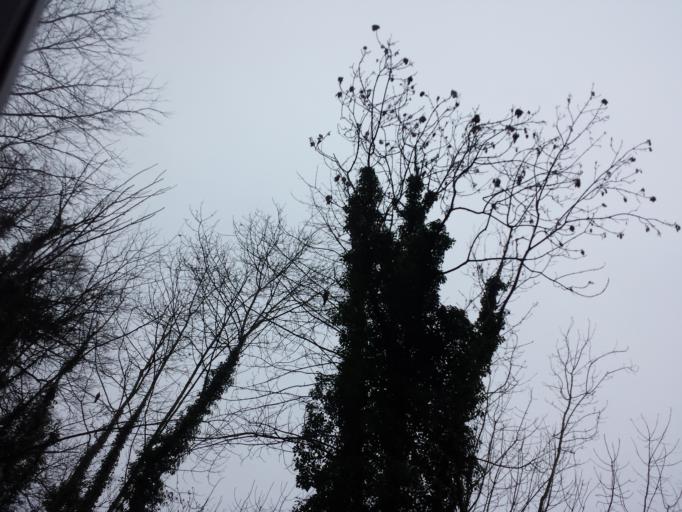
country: GB
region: England
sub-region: Bath and North East Somerset
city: Bath
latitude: 51.3805
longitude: -2.3513
